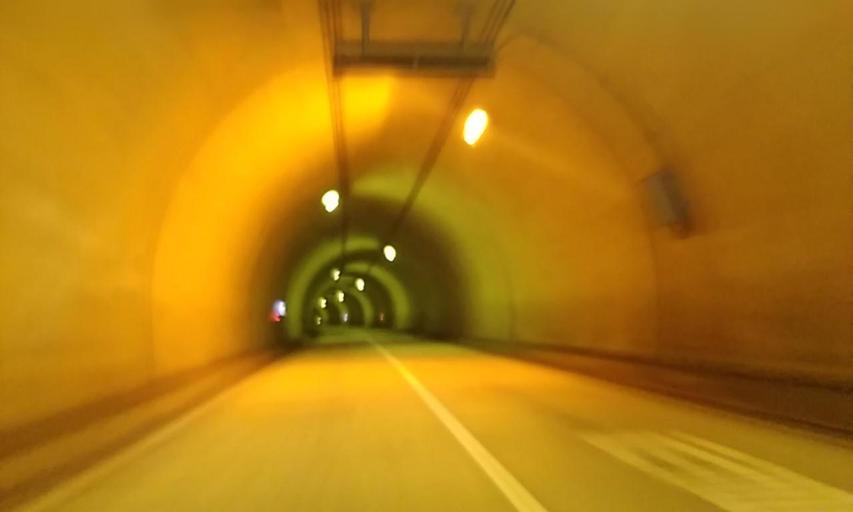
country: JP
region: Wakayama
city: Shingu
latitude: 33.8963
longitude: 135.8795
